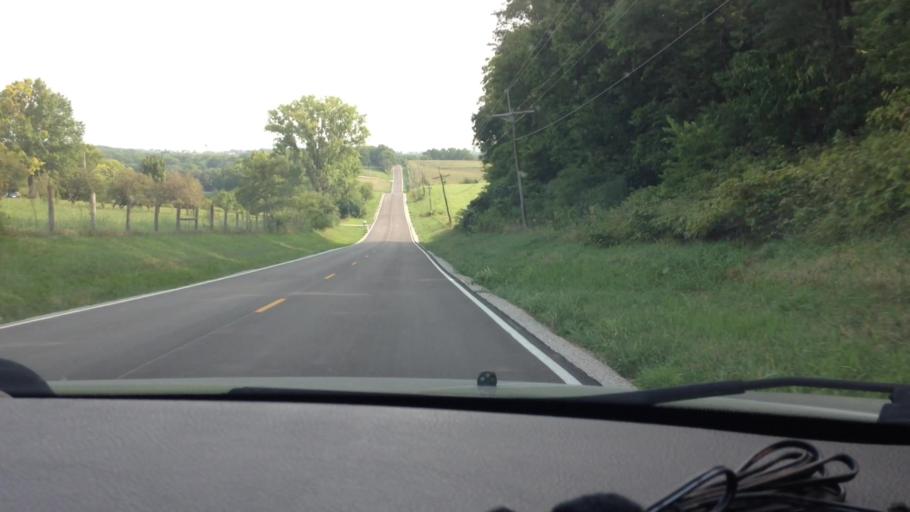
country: US
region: Missouri
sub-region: Platte County
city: Platte City
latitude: 39.3982
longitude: -94.7797
